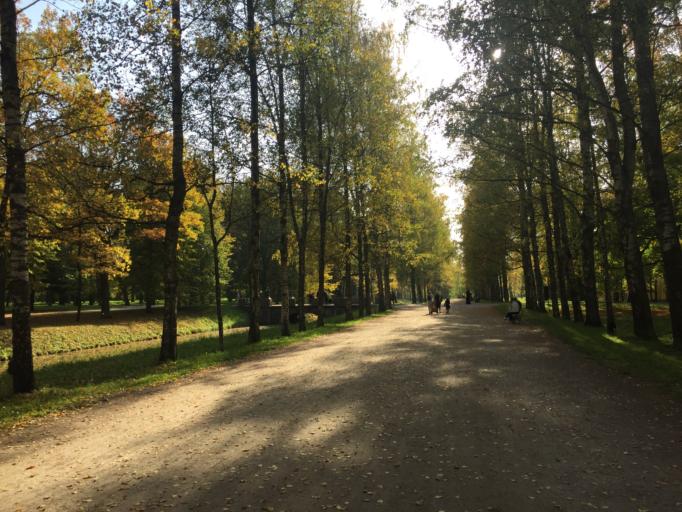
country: RU
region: St.-Petersburg
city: Pushkin
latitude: 59.7198
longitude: 30.3861
